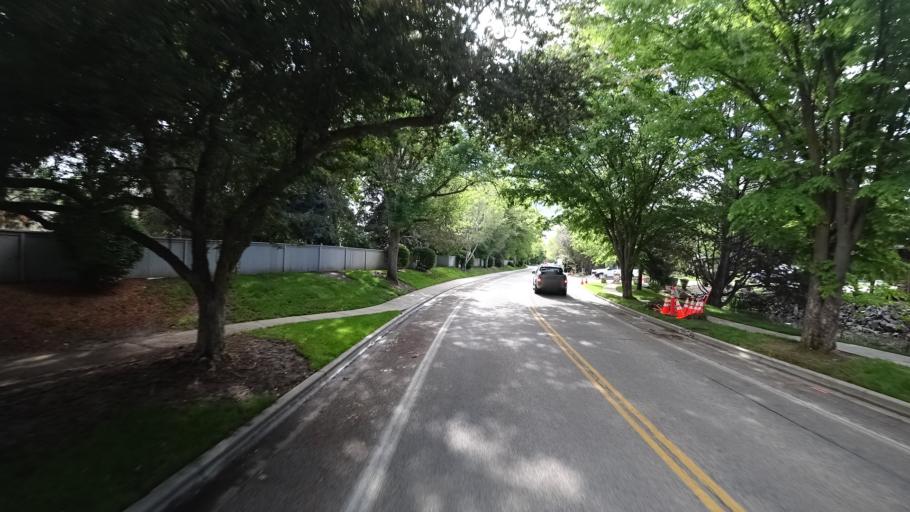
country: US
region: Idaho
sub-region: Ada County
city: Eagle
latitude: 43.6662
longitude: -116.2935
